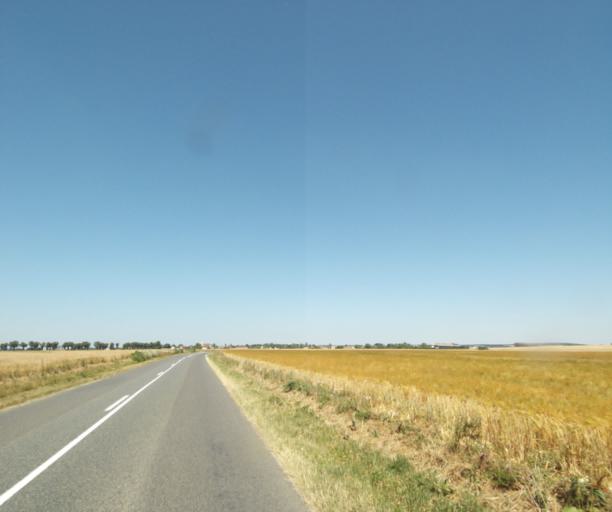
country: FR
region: Ile-de-France
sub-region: Departement de Seine-et-Marne
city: La Chapelle-la-Reine
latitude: 48.3067
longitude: 2.5593
